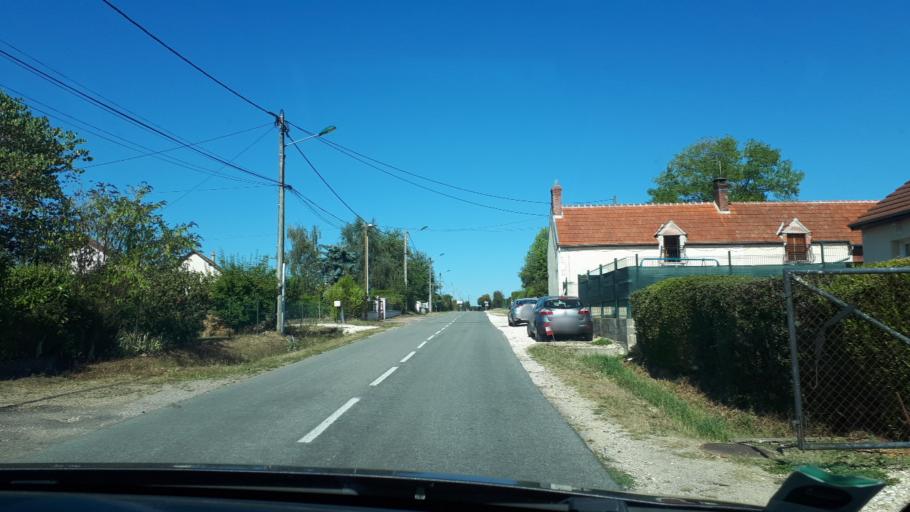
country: FR
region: Centre
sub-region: Departement du Loiret
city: Briare
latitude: 47.5875
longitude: 2.7329
